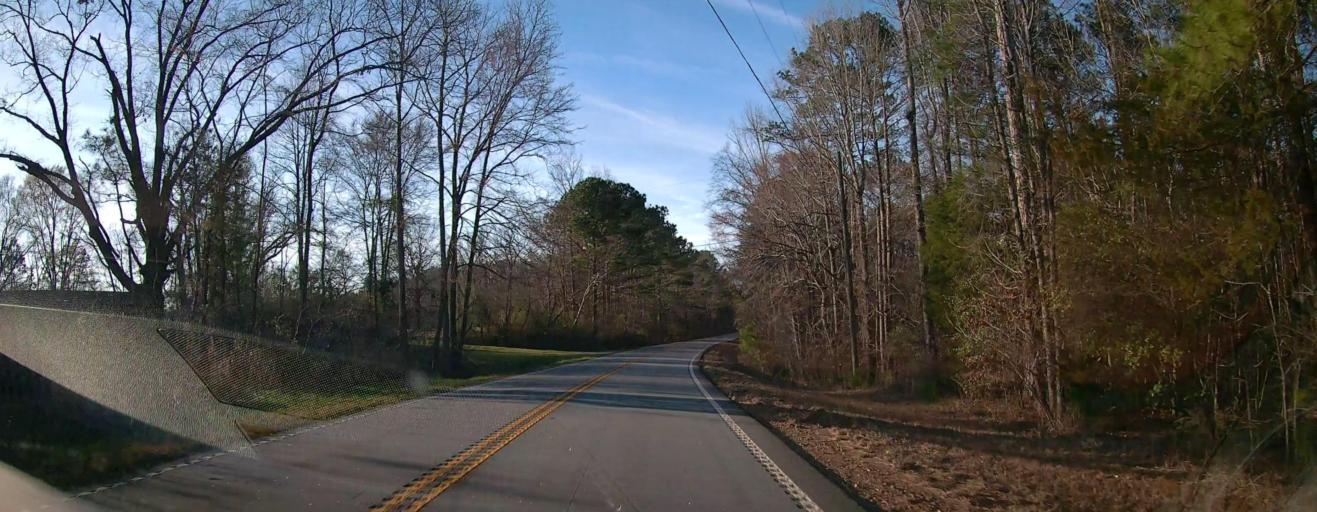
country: US
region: Alabama
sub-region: Chambers County
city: Valley
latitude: 32.7783
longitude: -85.0897
